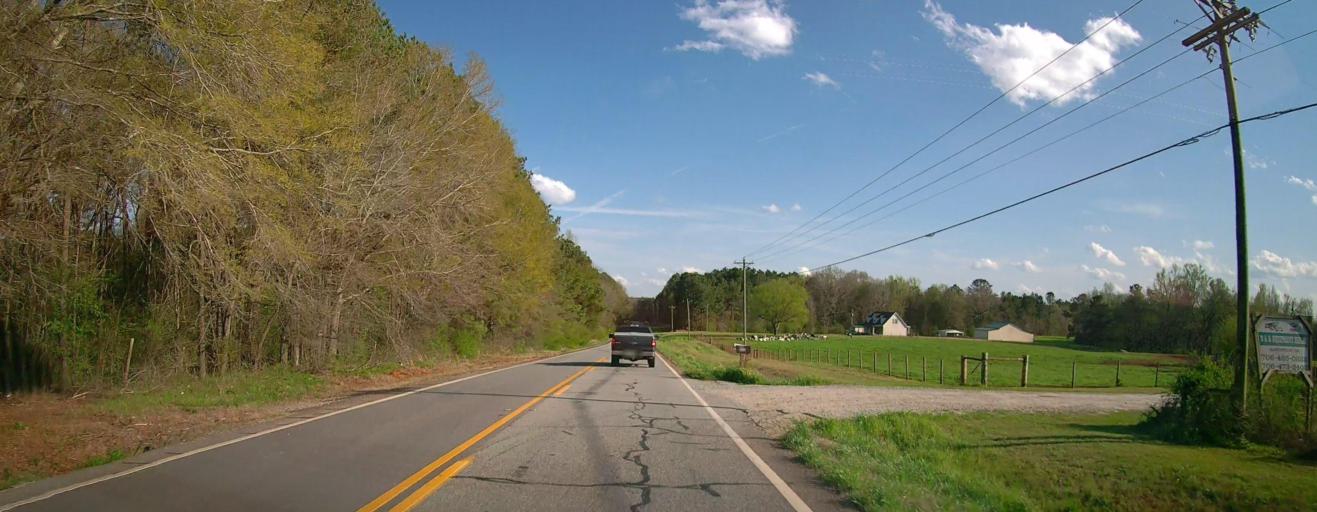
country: US
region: Georgia
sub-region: Putnam County
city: Eatonton
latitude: 33.1910
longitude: -83.4175
